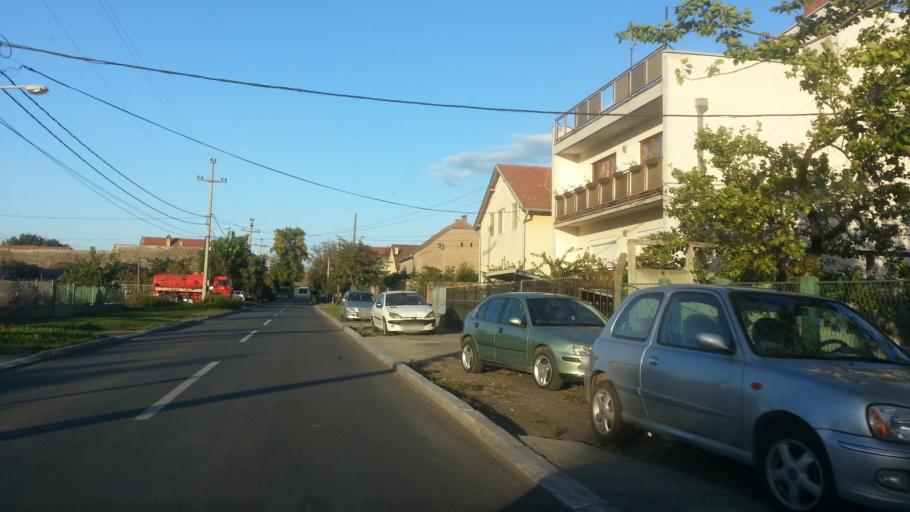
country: RS
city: Novi Banovci
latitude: 44.9011
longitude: 20.2737
